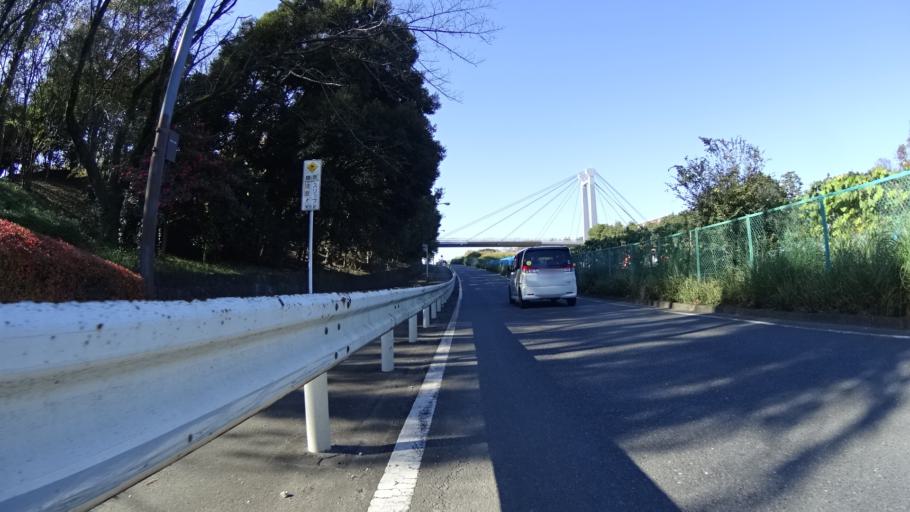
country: JP
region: Tokyo
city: Hino
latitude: 35.6099
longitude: 139.4327
